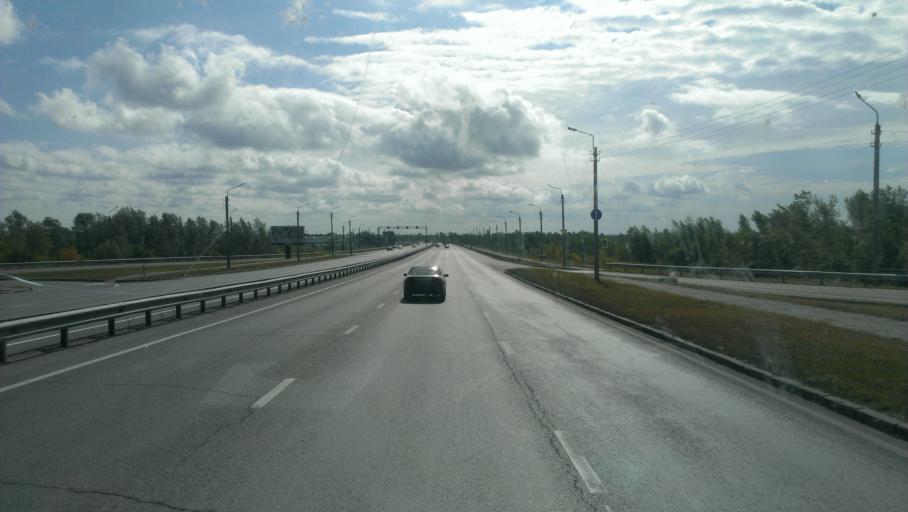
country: RU
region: Altai Krai
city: Zaton
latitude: 53.3195
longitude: 83.8146
